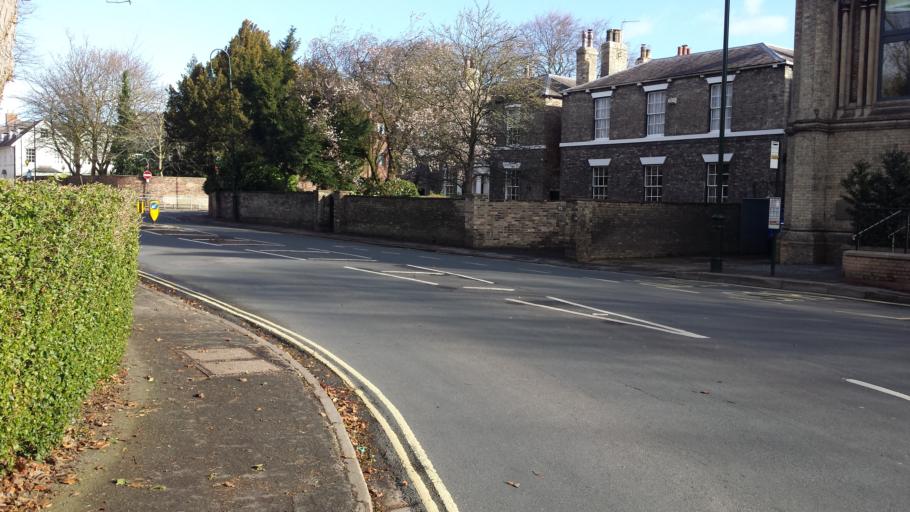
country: GB
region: England
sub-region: East Riding of Yorkshire
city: Beverley
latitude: 53.8397
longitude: -0.4310
